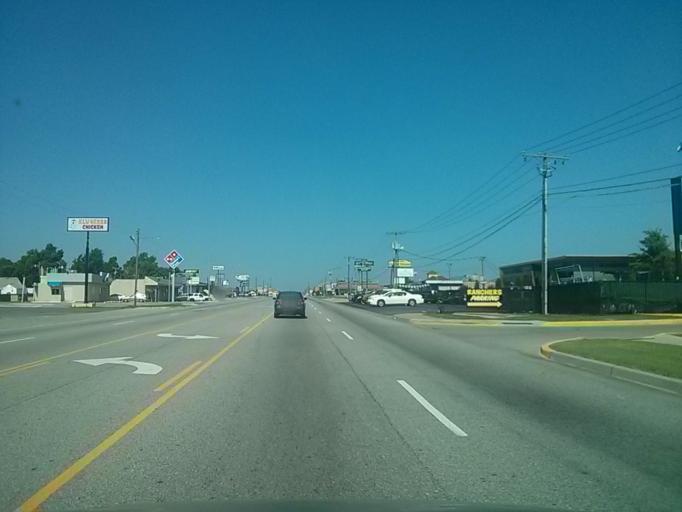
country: US
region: Oklahoma
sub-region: Tulsa County
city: Tulsa
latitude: 36.1608
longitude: -95.8970
